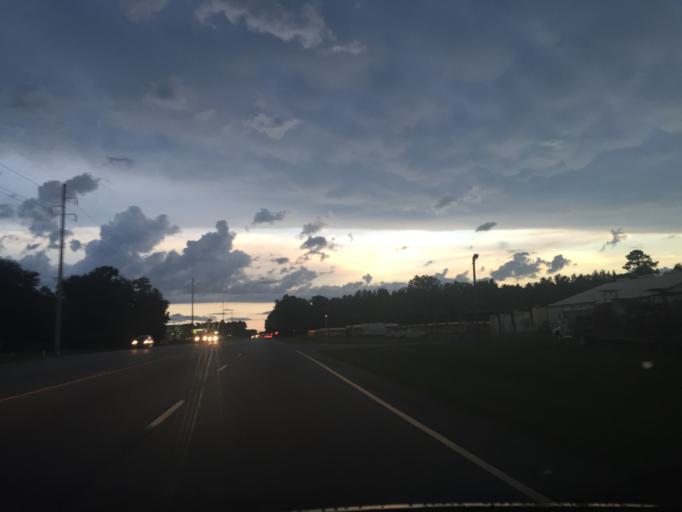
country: US
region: Georgia
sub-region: Liberty County
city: Hinesville
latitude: 31.8368
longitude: -81.5371
